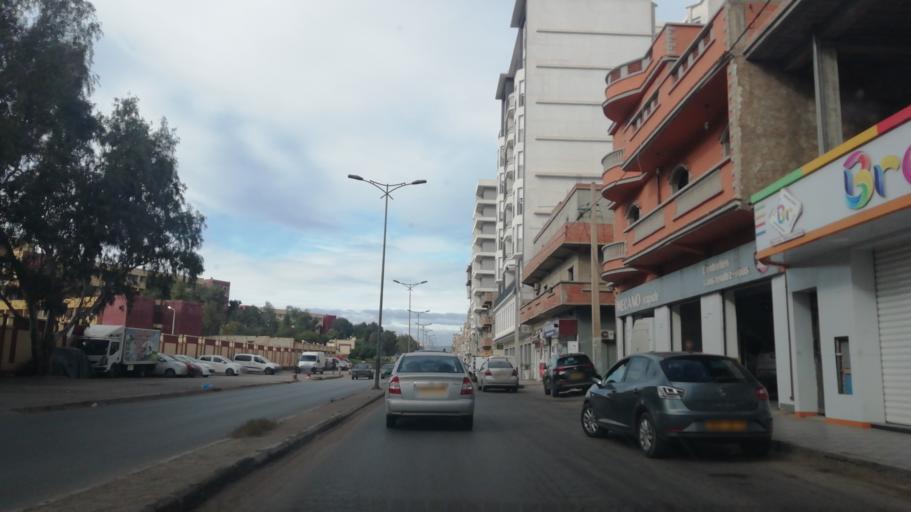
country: DZ
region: Oran
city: Bir el Djir
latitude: 35.7127
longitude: -0.5884
